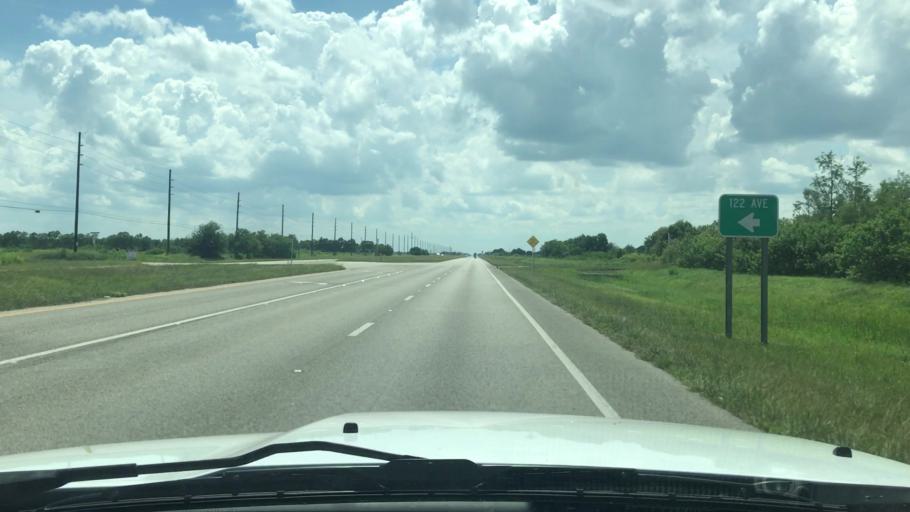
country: US
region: Florida
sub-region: Indian River County
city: West Vero Corridor
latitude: 27.6401
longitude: -80.5769
